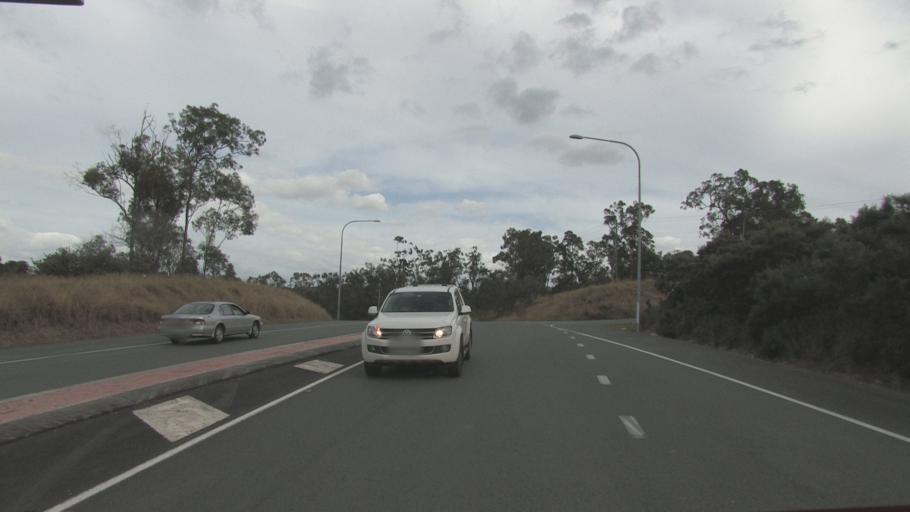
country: AU
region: Queensland
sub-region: Logan
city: Beenleigh
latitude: -27.7124
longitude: 153.1702
